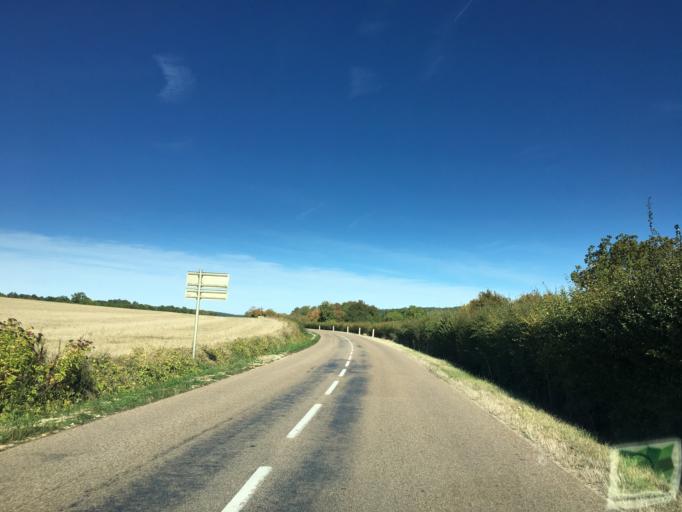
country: FR
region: Bourgogne
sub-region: Departement de l'Yonne
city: Vermenton
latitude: 47.6102
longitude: 3.6781
